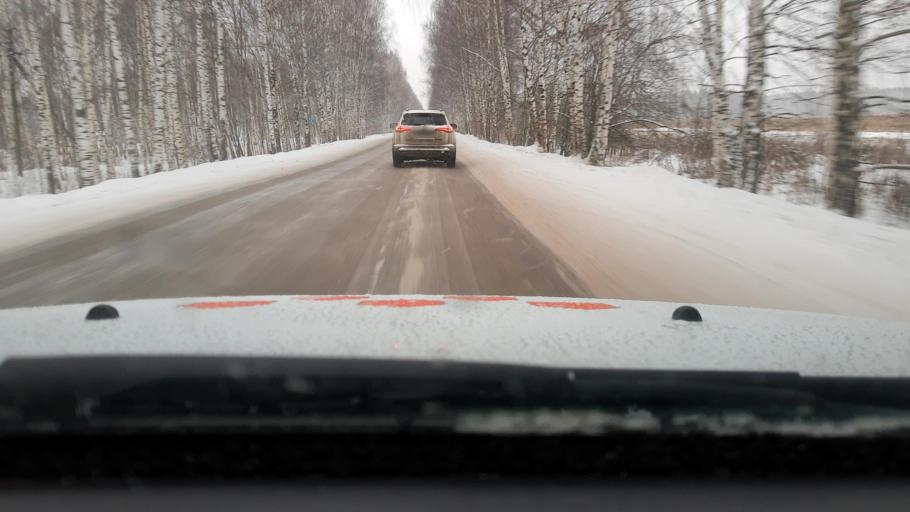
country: RU
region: Nizjnij Novgorod
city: Neklyudovo
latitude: 56.4804
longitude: 43.8710
